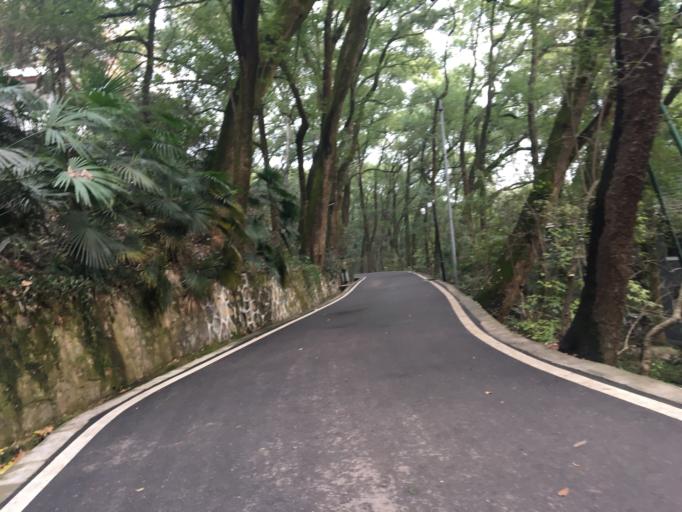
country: CN
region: Hubei
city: Guanshan
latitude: 30.5369
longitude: 114.3680
